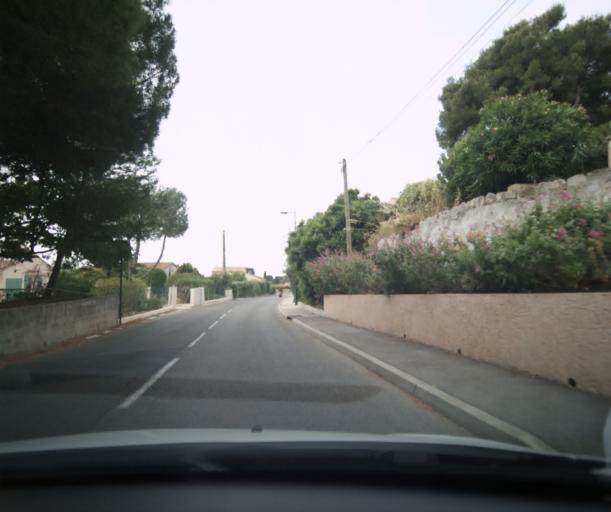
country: FR
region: Provence-Alpes-Cote d'Azur
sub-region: Departement du Var
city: Carqueiranne
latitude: 43.0980
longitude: 6.0800
